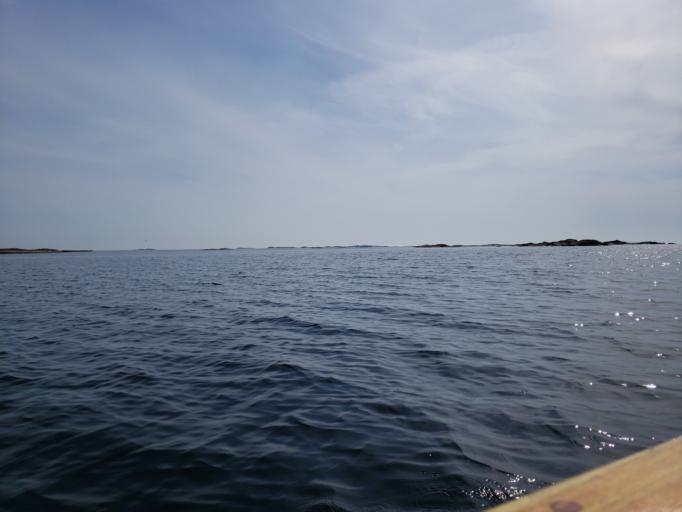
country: FI
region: Varsinais-Suomi
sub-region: Aboland-Turunmaa
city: Dragsfjaerd
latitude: 59.8394
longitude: 22.2015
